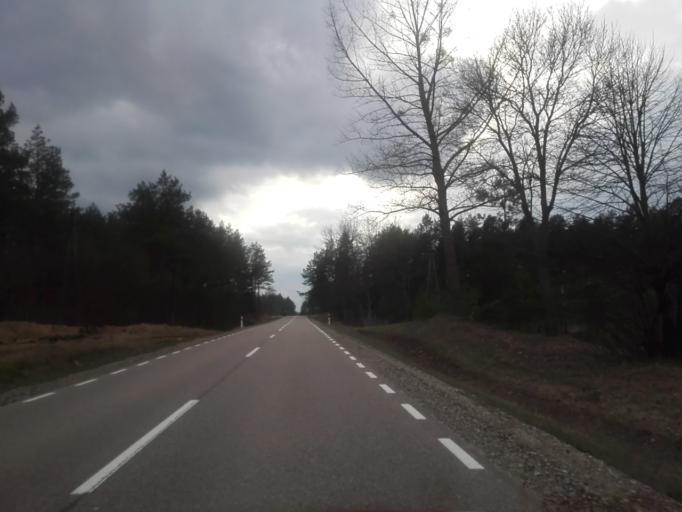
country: PL
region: Podlasie
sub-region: Powiat sejnenski
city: Krasnopol
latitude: 53.9534
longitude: 23.2098
